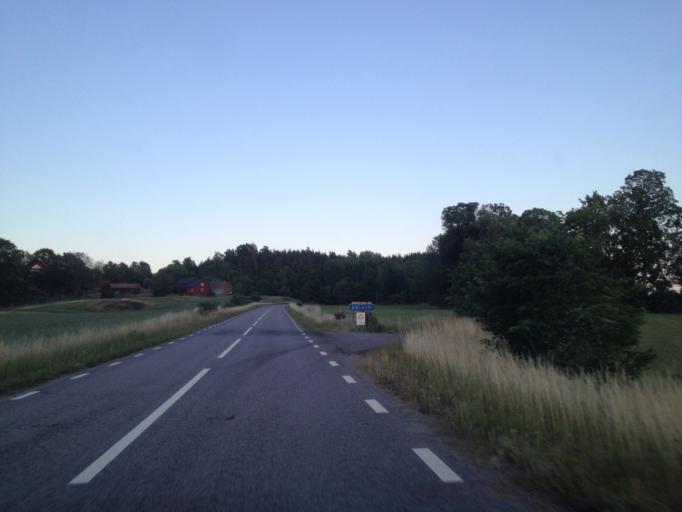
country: SE
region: Kalmar
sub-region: Vasterviks Kommun
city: Overum
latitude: 57.9943
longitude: 16.1825
